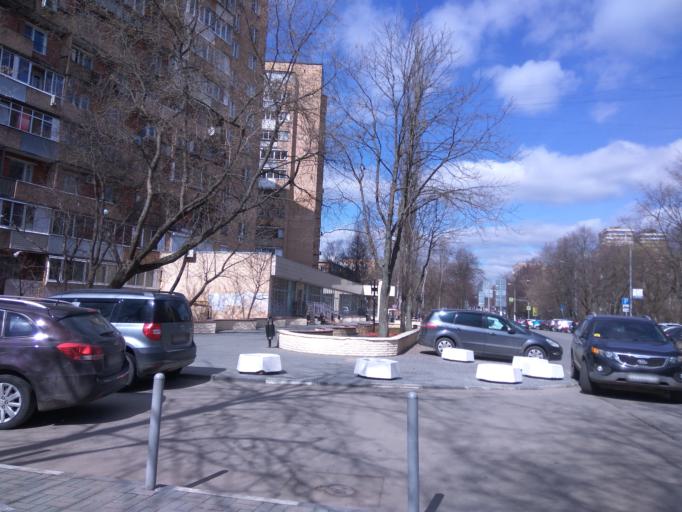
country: RU
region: Moskovskaya
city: Izmaylovo
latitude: 55.7898
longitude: 37.7995
